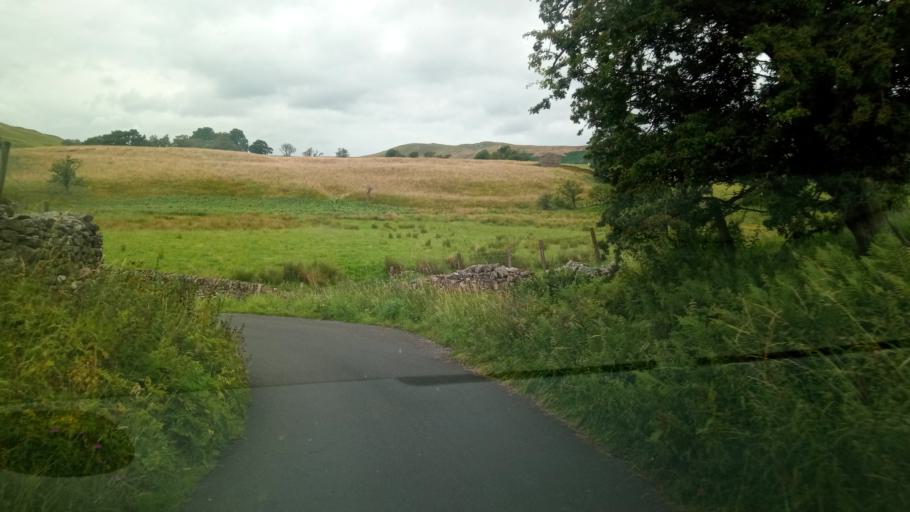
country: GB
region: England
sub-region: Cumbria
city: Kirkby Stephen
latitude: 54.4195
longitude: -2.3375
